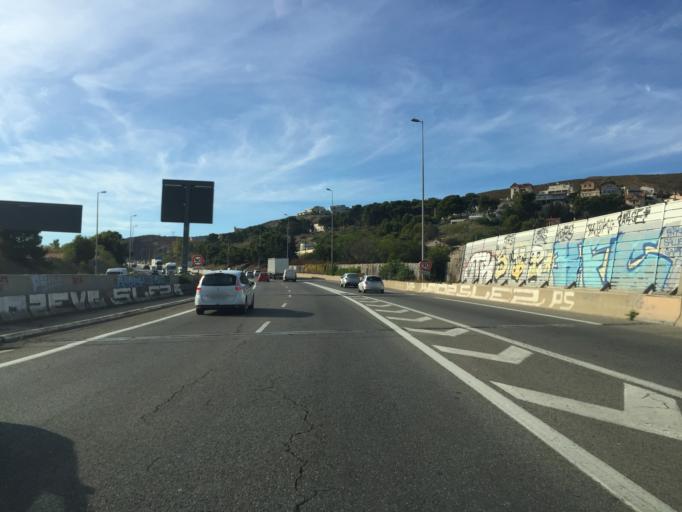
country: FR
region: Provence-Alpes-Cote d'Azur
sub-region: Departement des Bouches-du-Rhone
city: Marseille 16
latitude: 43.3656
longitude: 5.3381
